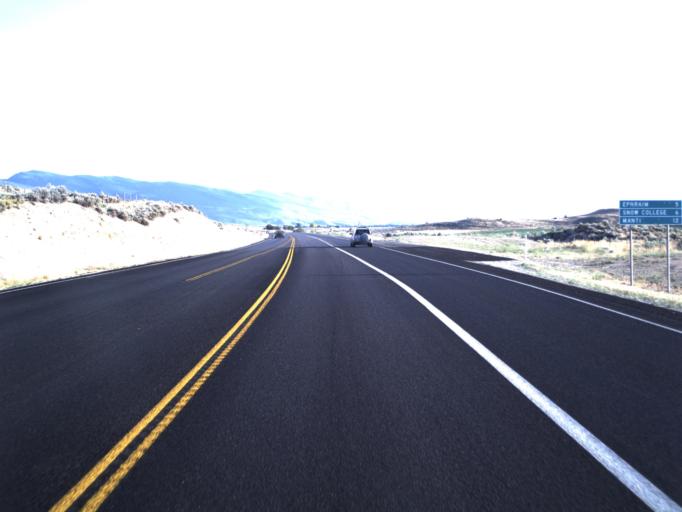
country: US
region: Utah
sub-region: Sanpete County
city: Ephraim
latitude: 39.4210
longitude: -111.5593
